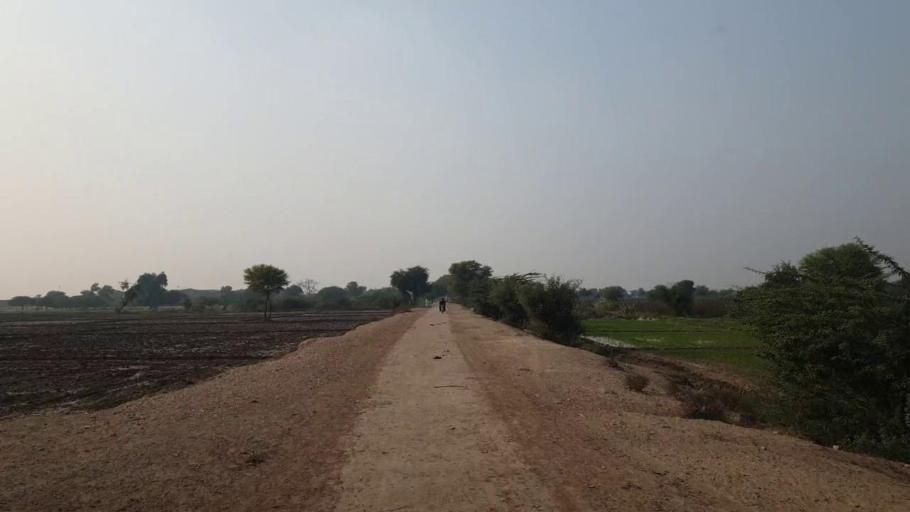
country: PK
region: Sindh
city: Bhan
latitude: 26.5597
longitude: 67.7081
